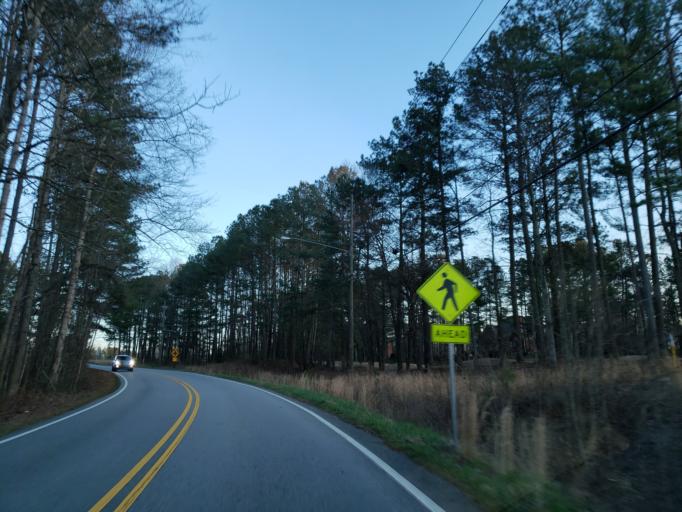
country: US
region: Georgia
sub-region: Cobb County
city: Acworth
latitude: 33.9953
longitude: -84.7258
